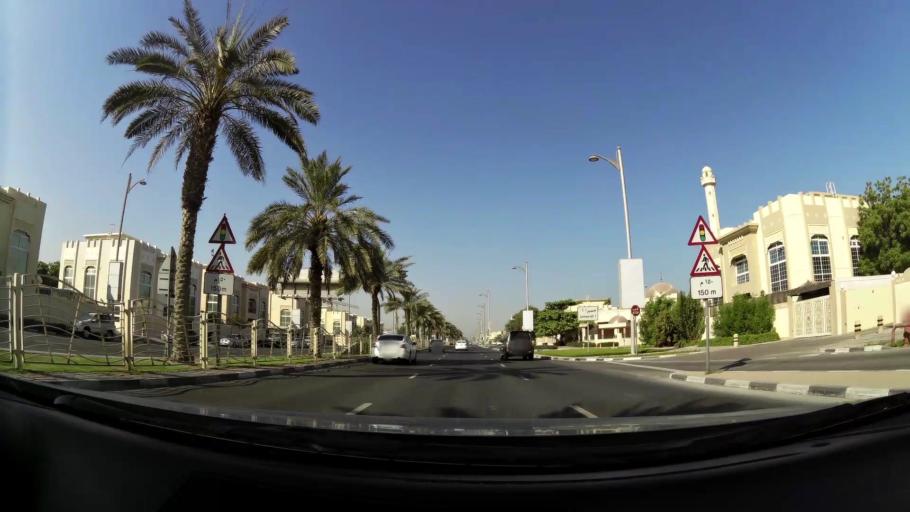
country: AE
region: Dubai
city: Dubai
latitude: 25.2134
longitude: 55.2493
